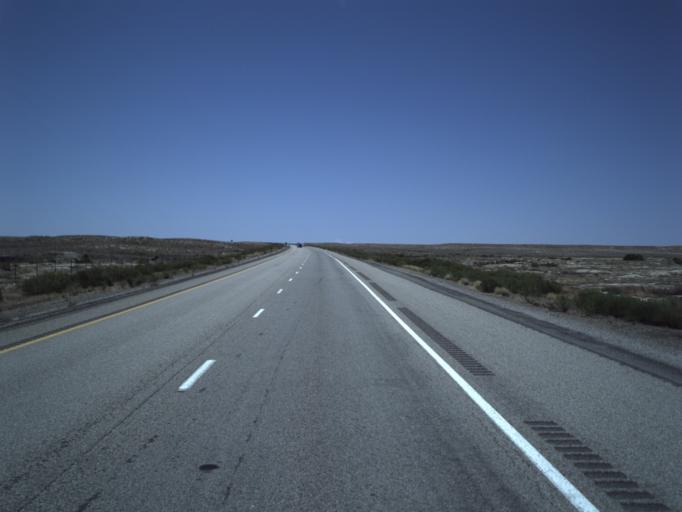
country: US
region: Utah
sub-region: Grand County
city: Moab
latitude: 38.9669
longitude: -109.3718
